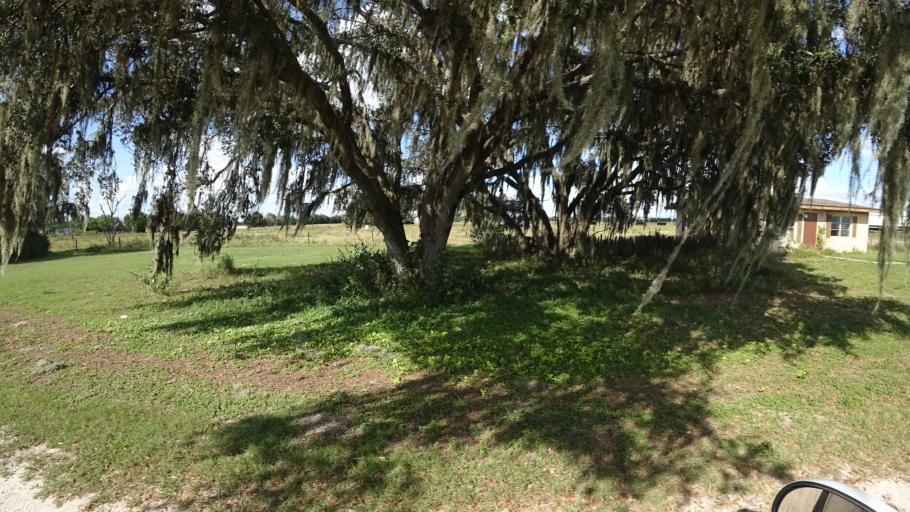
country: US
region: Florida
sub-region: DeSoto County
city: Nocatee
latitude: 27.2907
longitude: -82.1124
